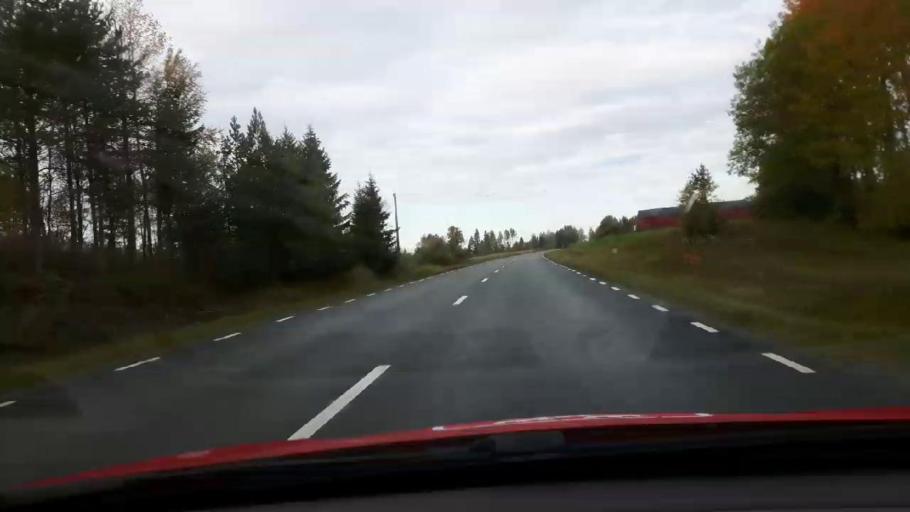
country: SE
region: Jaemtland
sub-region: Krokoms Kommun
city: Krokom
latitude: 63.1097
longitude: 14.2940
